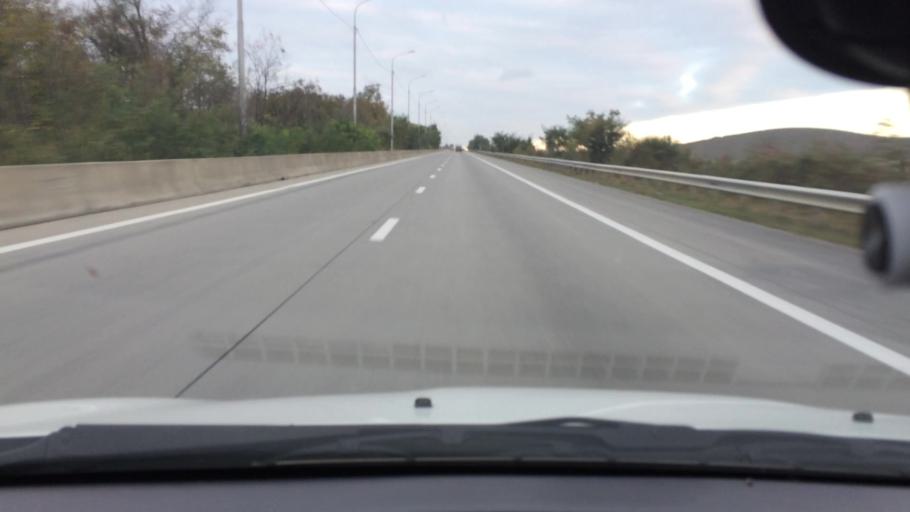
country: GE
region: Shida Kartli
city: Kaspi
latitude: 41.9743
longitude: 44.4454
